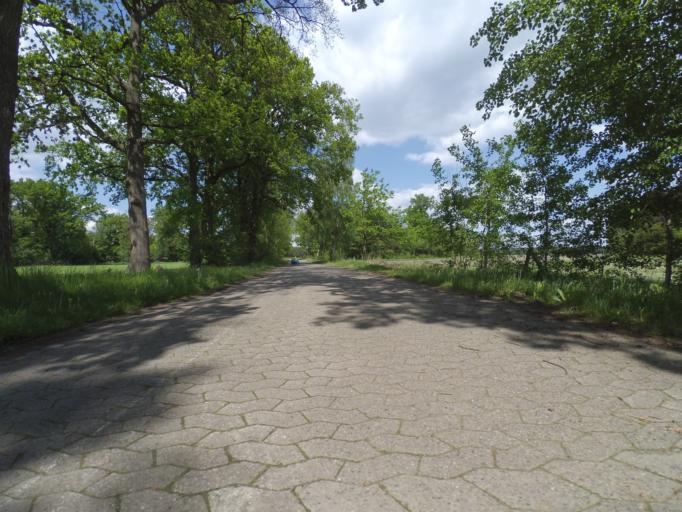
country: DE
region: Lower Saxony
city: Ummern
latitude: 52.6061
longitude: 10.4573
